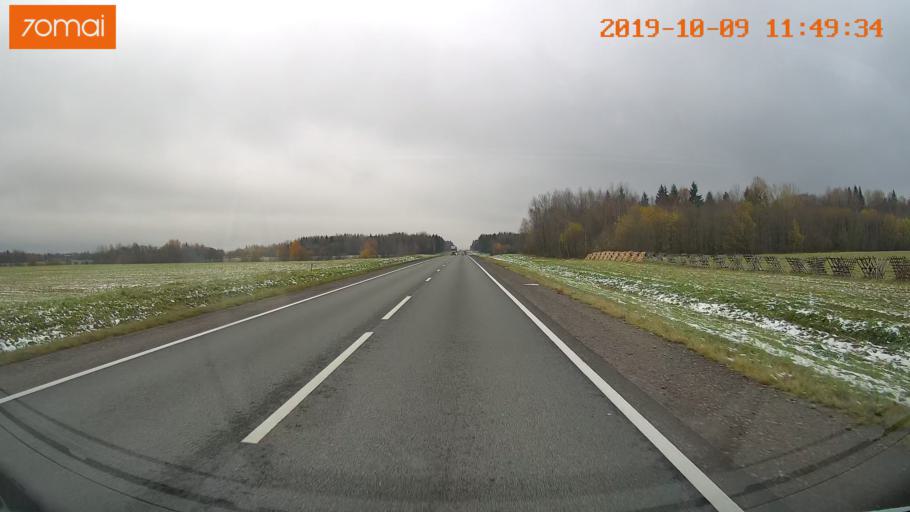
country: RU
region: Vologda
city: Gryazovets
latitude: 58.8168
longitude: 40.2321
